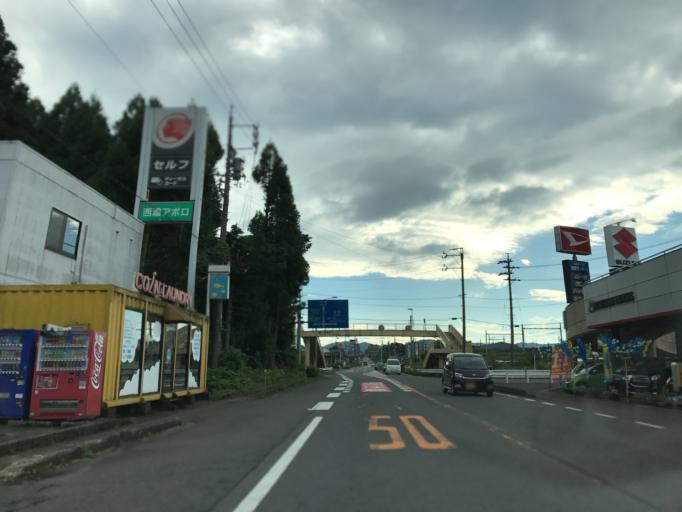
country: JP
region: Gifu
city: Tarui
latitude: 35.3654
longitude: 136.4872
